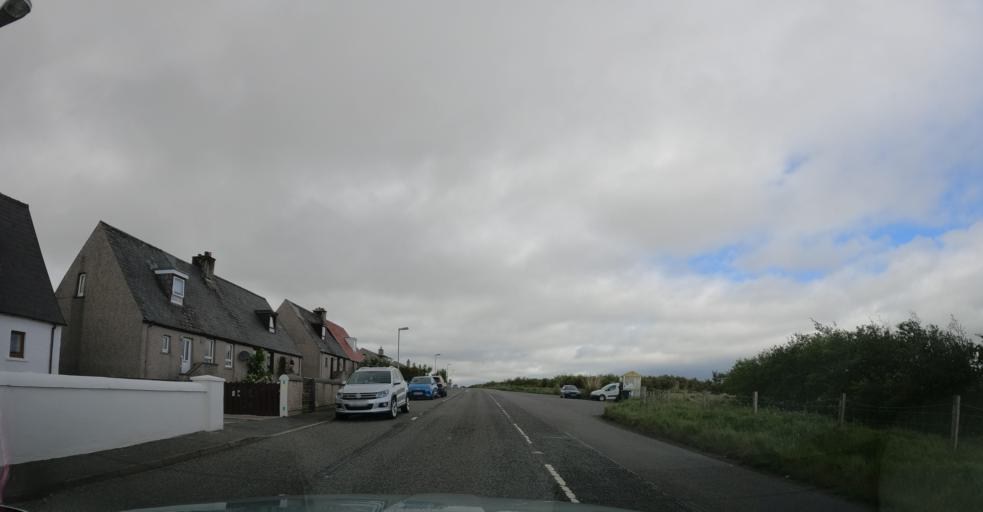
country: GB
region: Scotland
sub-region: Eilean Siar
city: Stornoway
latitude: 58.1557
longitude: -6.4977
